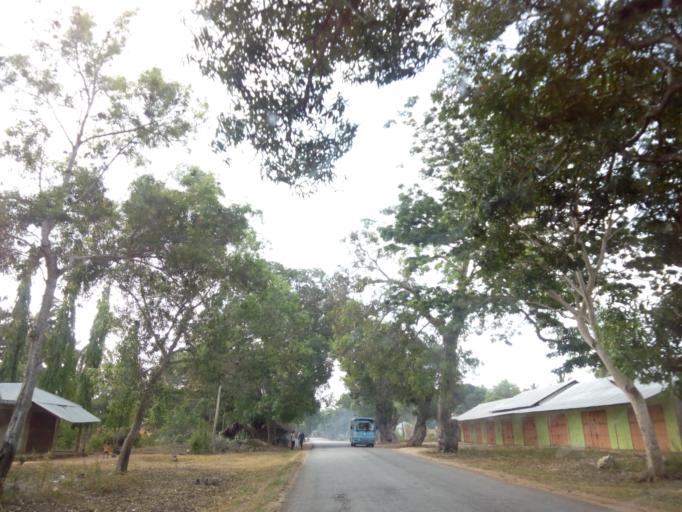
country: TZ
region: Zanzibar Central/South
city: Koani
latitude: -6.2678
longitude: 39.3431
